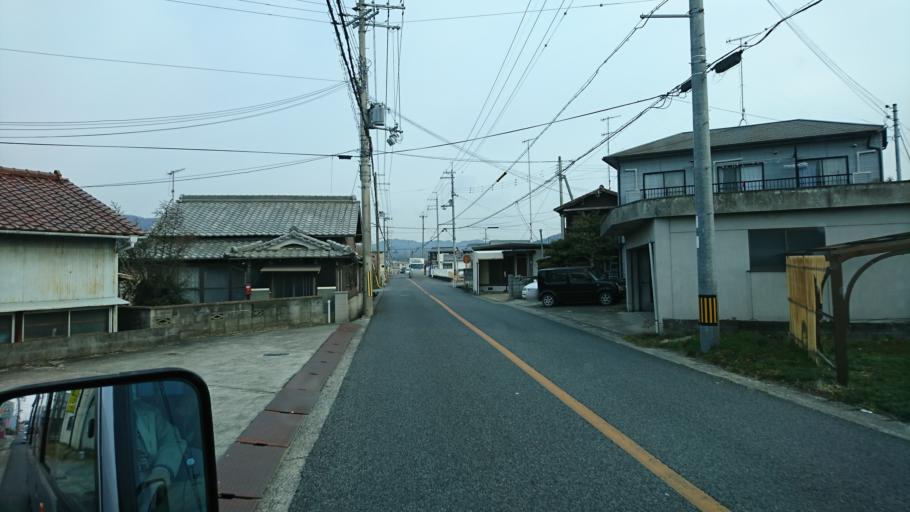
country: JP
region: Hyogo
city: Kakogawacho-honmachi
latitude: 34.8116
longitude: 134.8182
